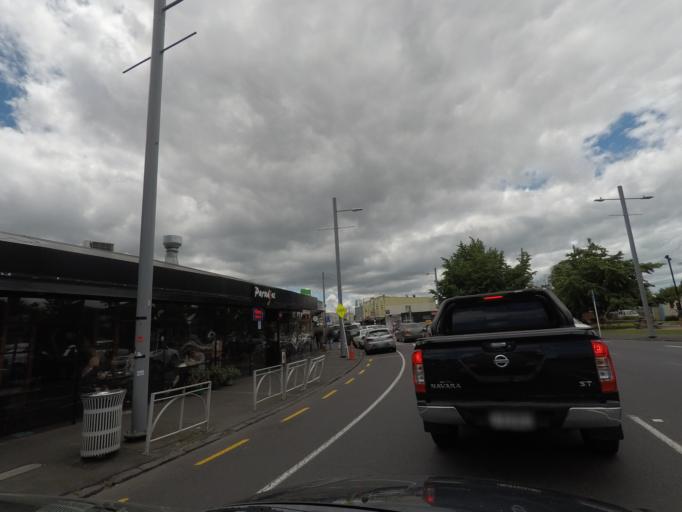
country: NZ
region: Auckland
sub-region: Auckland
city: Auckland
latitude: -36.8931
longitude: 174.7365
